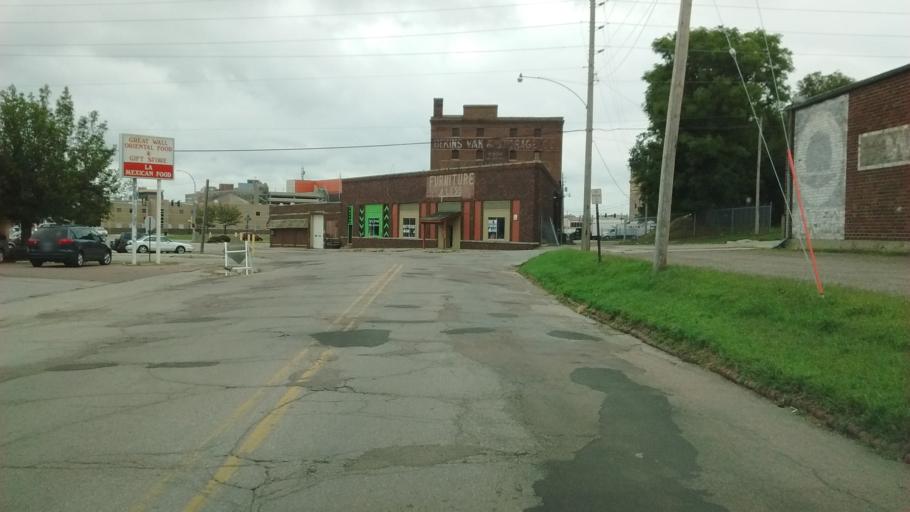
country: US
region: Iowa
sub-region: Woodbury County
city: Sioux City
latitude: 42.4965
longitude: -96.4126
